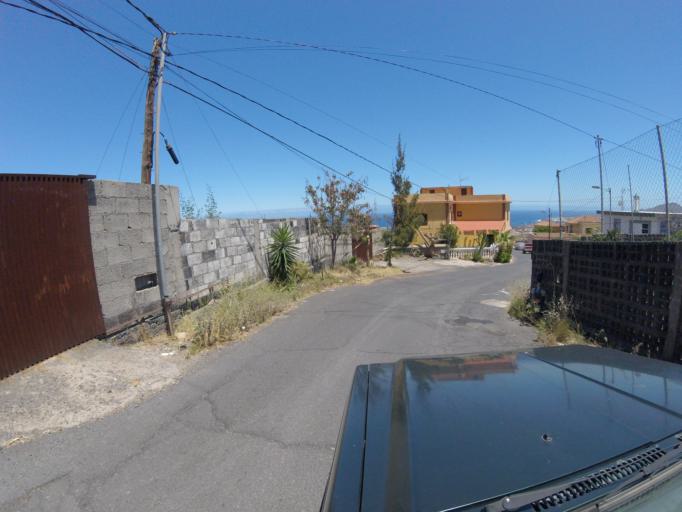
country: ES
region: Canary Islands
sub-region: Provincia de Santa Cruz de Tenerife
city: Candelaria
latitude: 28.3654
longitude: -16.3784
